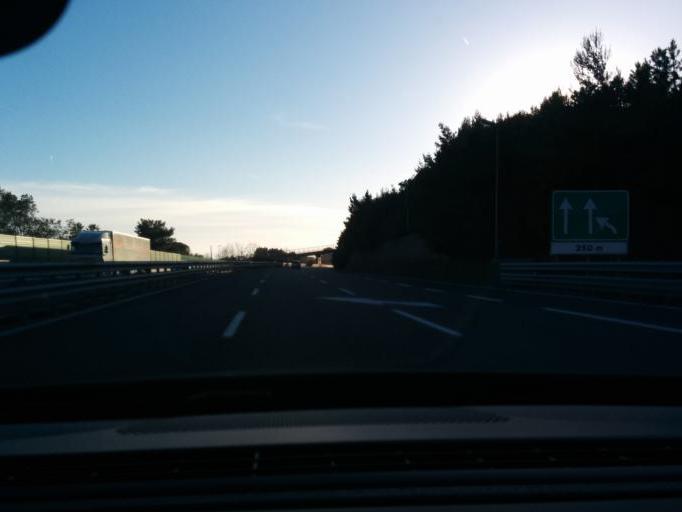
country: IT
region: Liguria
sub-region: Provincia di Savona
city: Varazze
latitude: 44.3678
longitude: 8.6037
